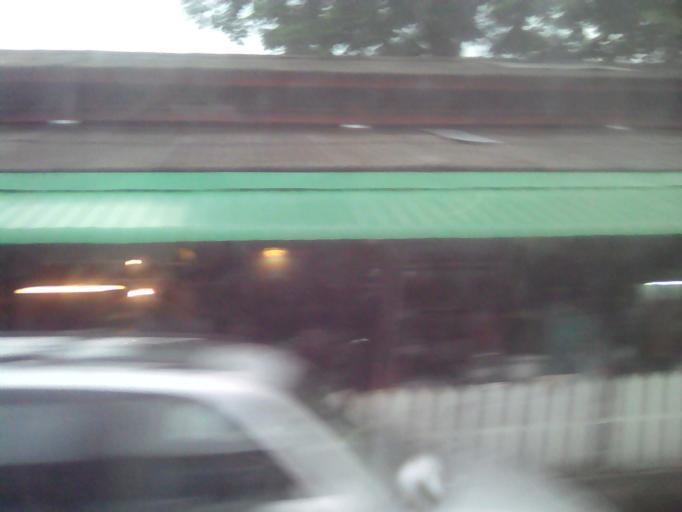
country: MY
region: Penang
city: Butterworth
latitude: 5.3979
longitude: 100.3705
